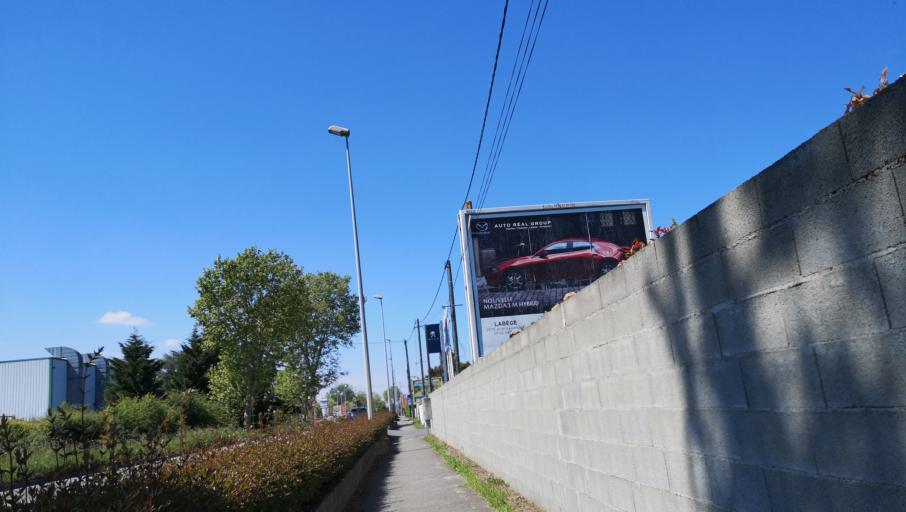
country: FR
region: Midi-Pyrenees
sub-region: Departement de la Haute-Garonne
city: Beauzelle
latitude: 43.6679
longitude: 1.3695
